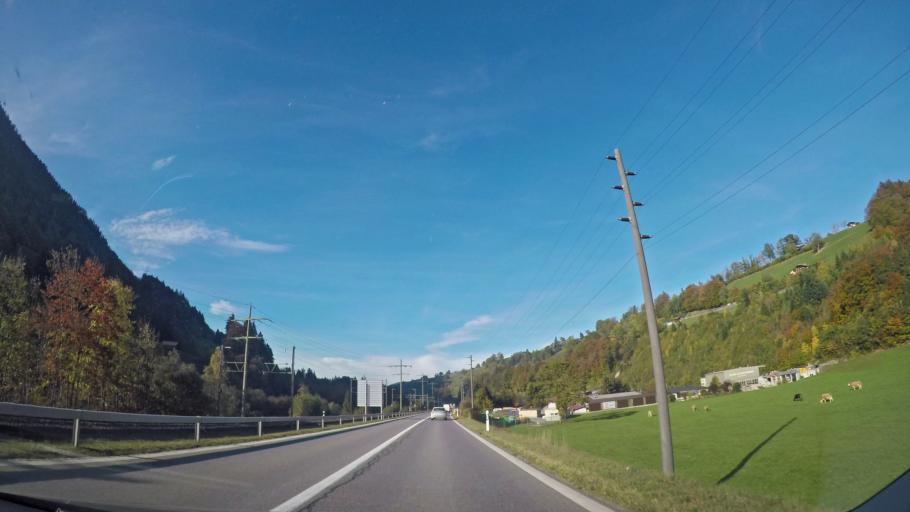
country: CH
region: Bern
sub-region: Frutigen-Niedersimmental District
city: Aeschi
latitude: 46.6406
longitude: 7.6912
